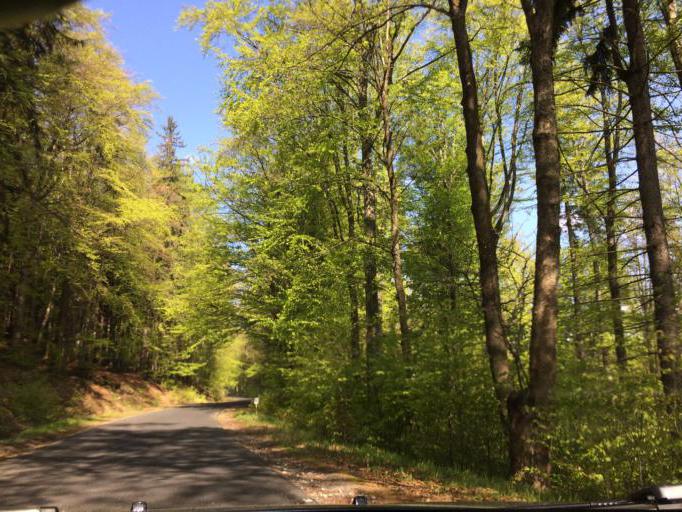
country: PL
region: Lower Silesian Voivodeship
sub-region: Powiat klodzki
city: Jugow
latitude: 50.6663
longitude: 16.5282
